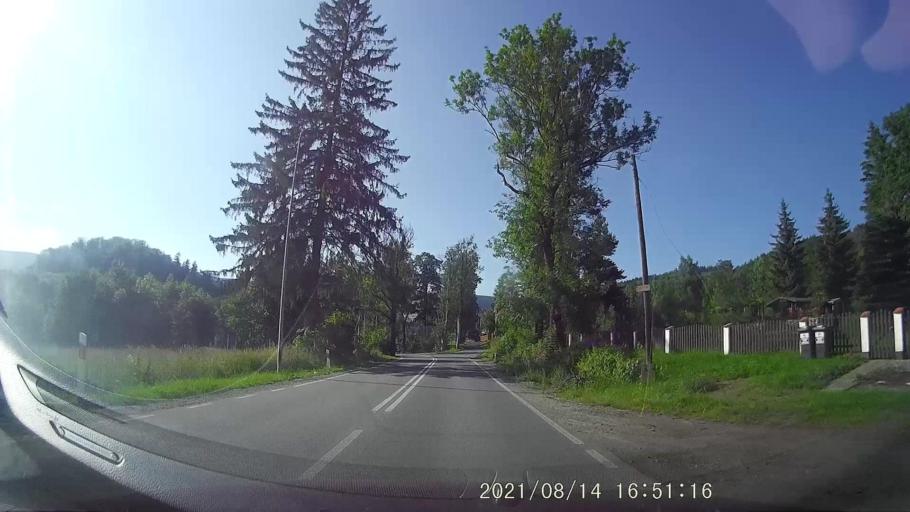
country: PL
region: Lower Silesian Voivodeship
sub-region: Powiat jeleniogorski
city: Kowary
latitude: 50.7761
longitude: 15.9155
